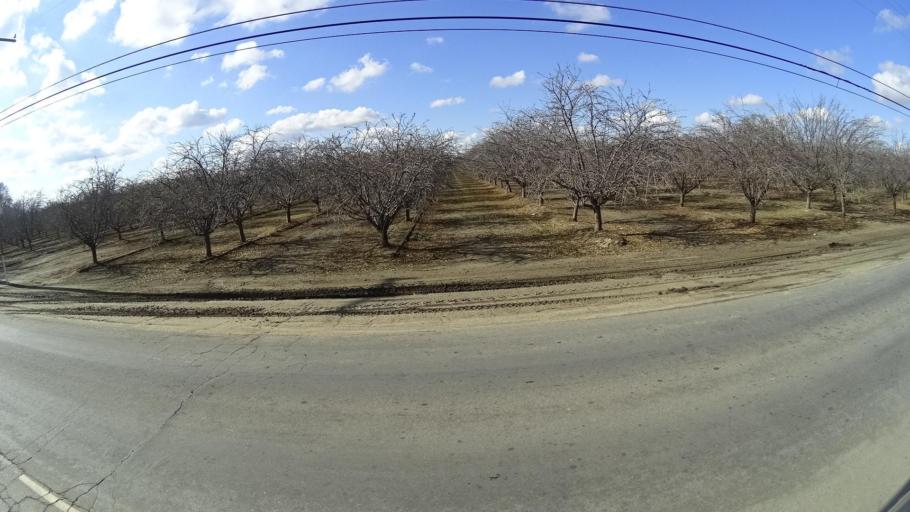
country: US
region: California
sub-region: Kern County
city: McFarland
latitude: 35.7160
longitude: -119.2408
